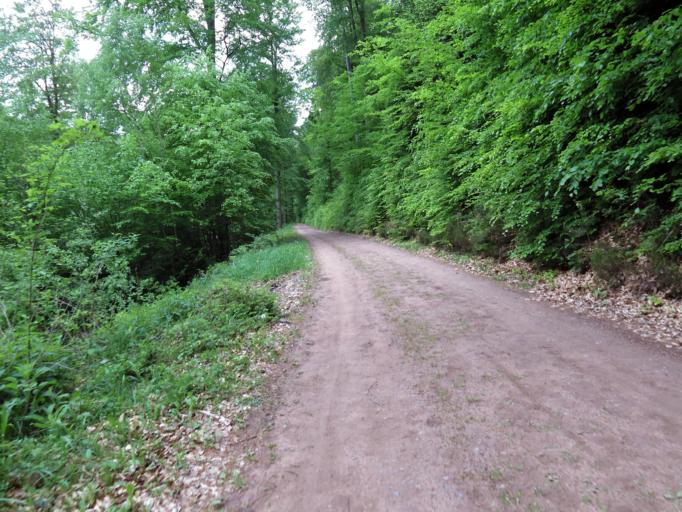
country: DE
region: Rheinland-Pfalz
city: Neidenfels
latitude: 49.4097
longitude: 8.0612
